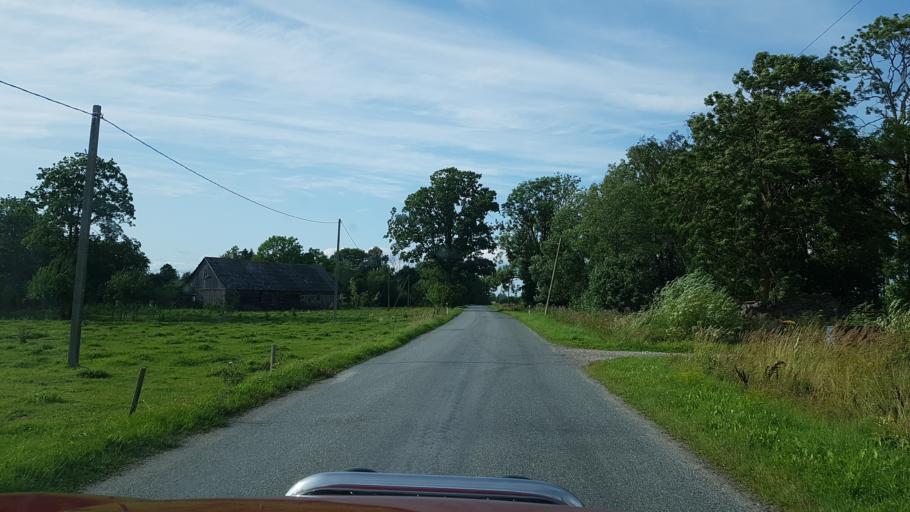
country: EE
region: Laeaene
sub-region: Lihula vald
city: Lihula
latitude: 58.4490
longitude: 23.9982
